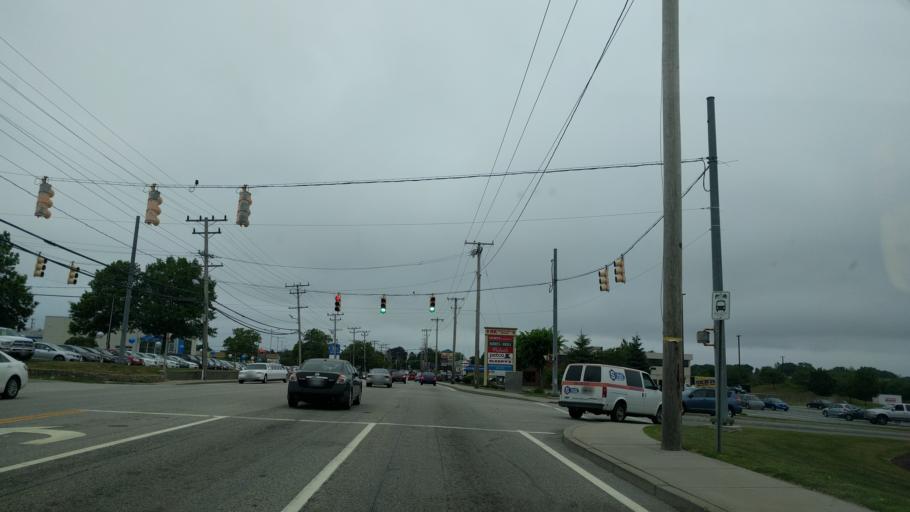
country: US
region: Rhode Island
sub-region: Newport County
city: Middletown
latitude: 41.5344
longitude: -71.2926
